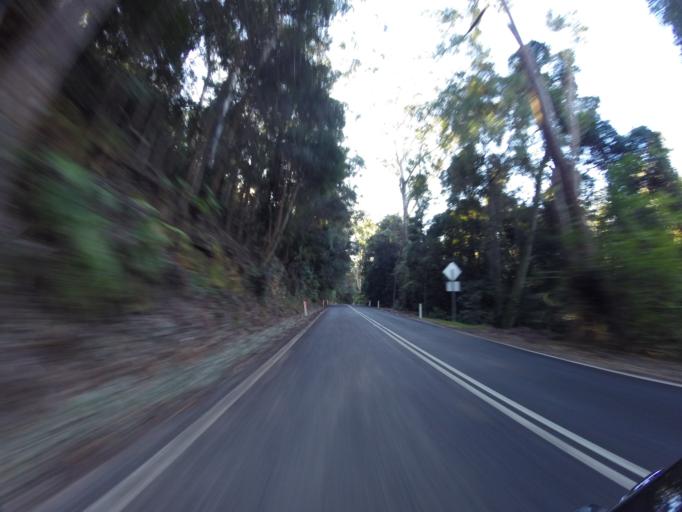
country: AU
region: New South Wales
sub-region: Wollongong
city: Helensburgh
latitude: -34.1864
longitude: 151.0151
